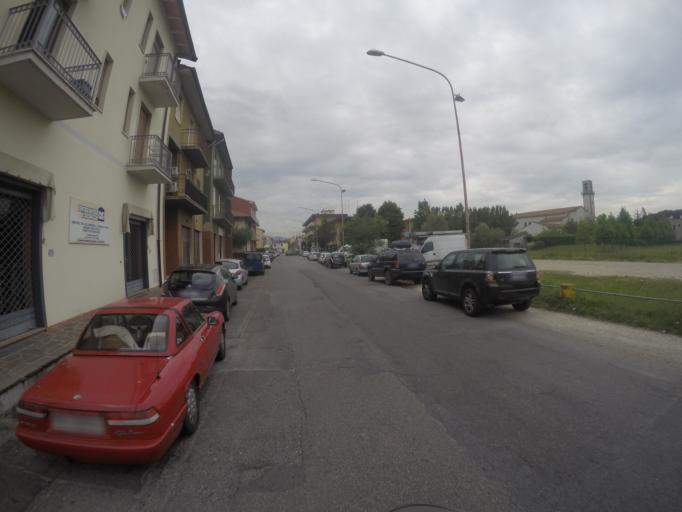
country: IT
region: Tuscany
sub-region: Provincia di Prato
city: Prato
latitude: 43.8960
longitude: 11.0683
